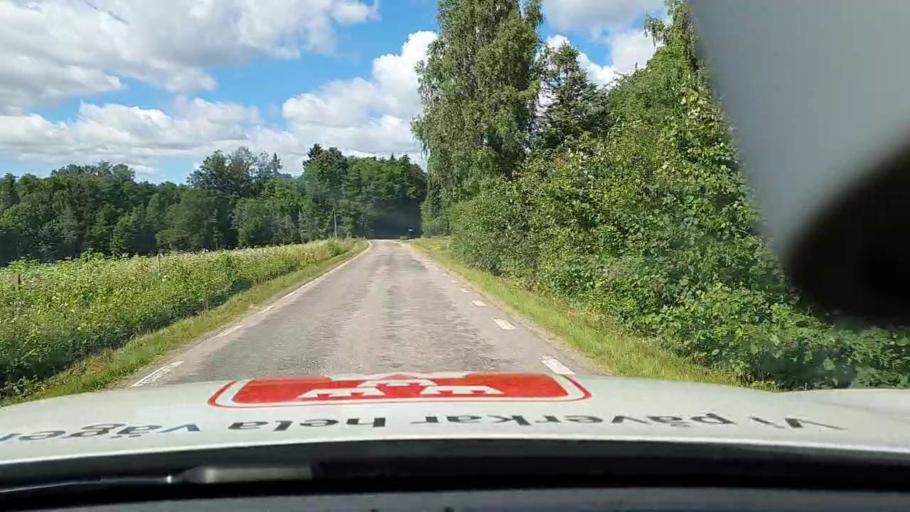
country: SE
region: Vaestra Goetaland
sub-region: Karlsborgs Kommun
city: Molltorp
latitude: 58.5901
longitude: 14.2664
